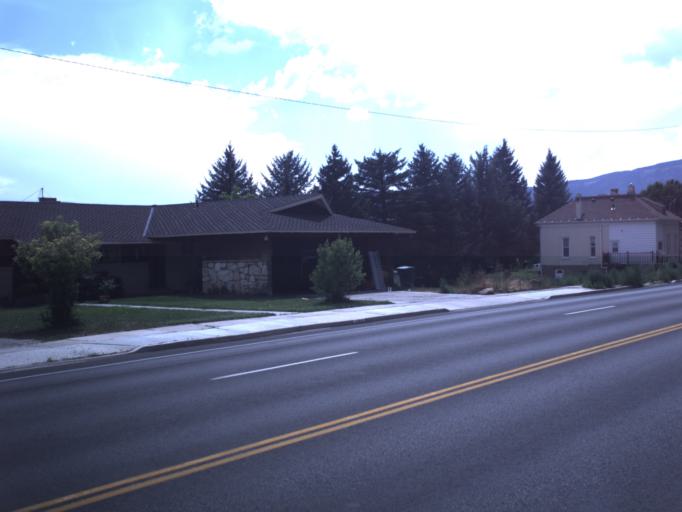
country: US
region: Utah
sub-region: Sanpete County
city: Moroni
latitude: 39.5250
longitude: -111.5805
